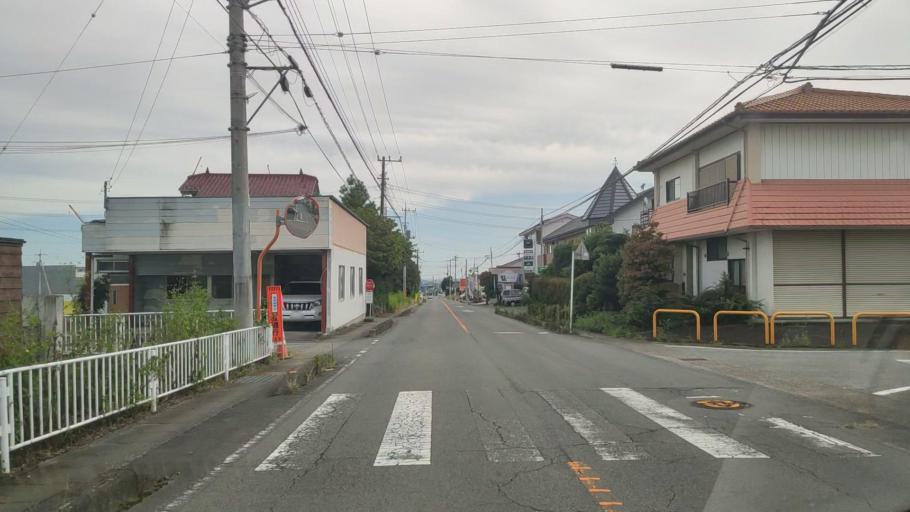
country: JP
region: Gunma
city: Kanekomachi
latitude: 36.3826
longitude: 138.9636
